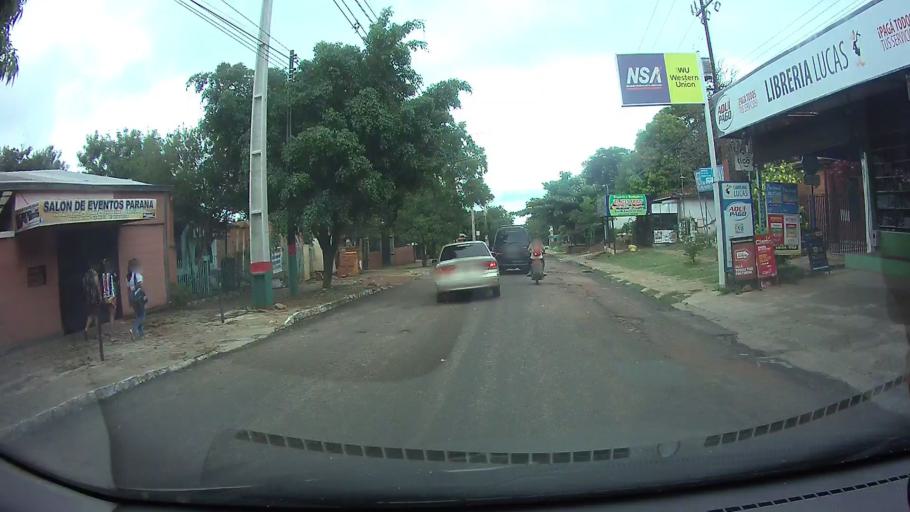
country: PY
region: Cordillera
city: Altos
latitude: -25.2646
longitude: -57.2490
